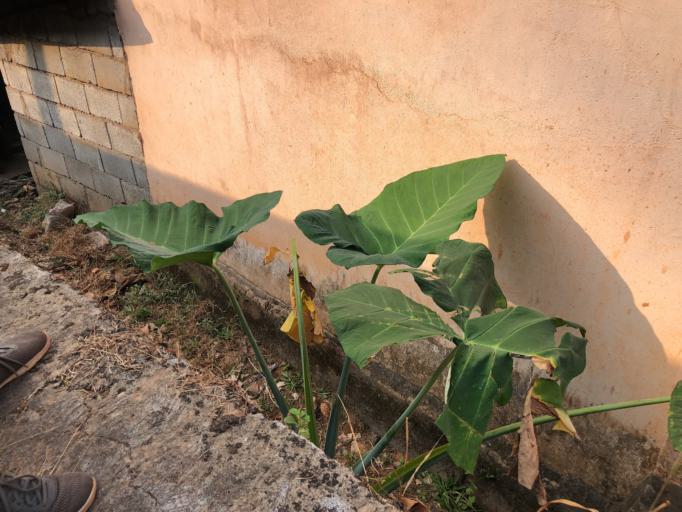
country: IN
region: Karnataka
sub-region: Dakshina Kannada
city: Mangalore
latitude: 12.8723
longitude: 74.8934
